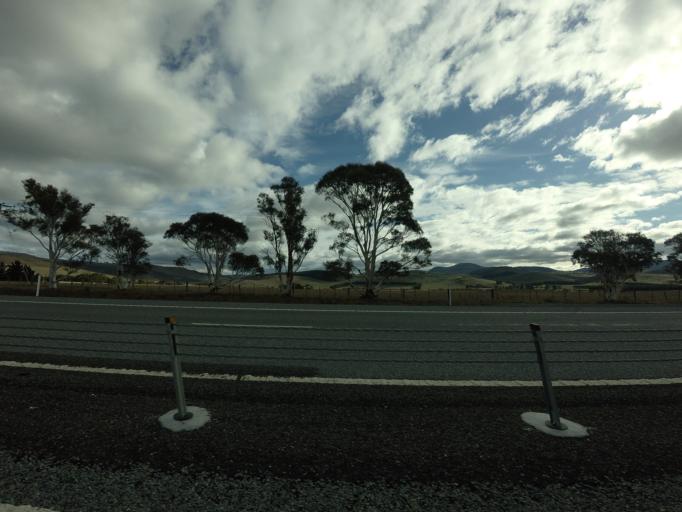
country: AU
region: Tasmania
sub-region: Brighton
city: Bridgewater
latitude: -42.4973
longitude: 147.1863
